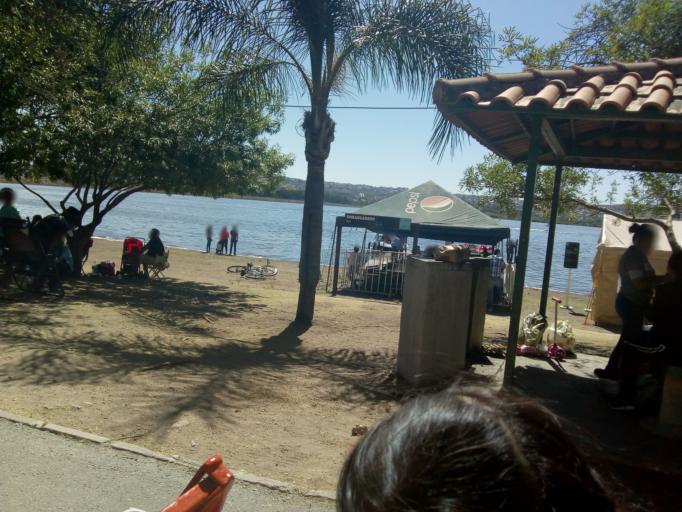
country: MX
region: Guanajuato
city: Leon
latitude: 21.1765
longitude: -101.6795
